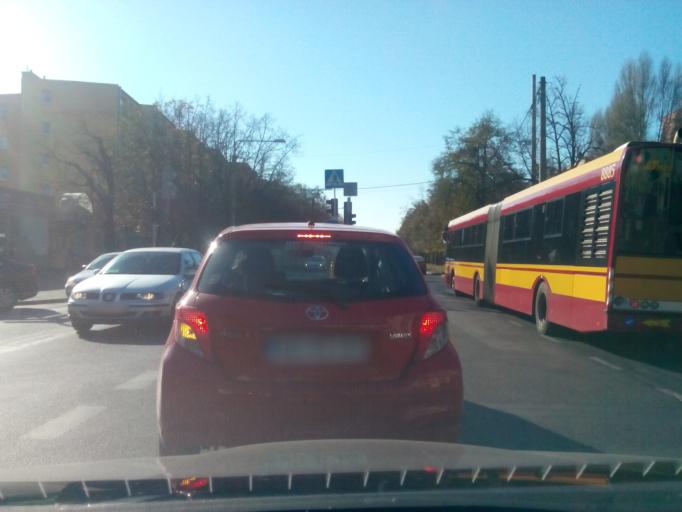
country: PL
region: Masovian Voivodeship
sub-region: Powiat pruszkowski
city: Pruszkow
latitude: 52.1625
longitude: 20.8034
